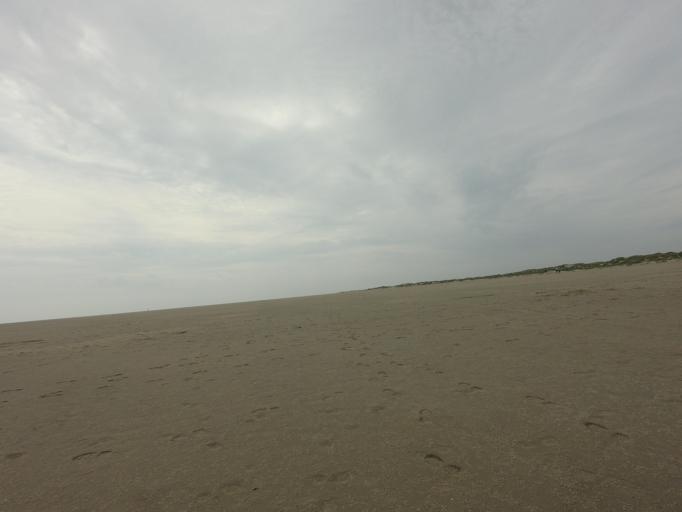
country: NL
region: North Holland
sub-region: Gemeente Den Helder
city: Den Helder
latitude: 52.9928
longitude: 4.7402
